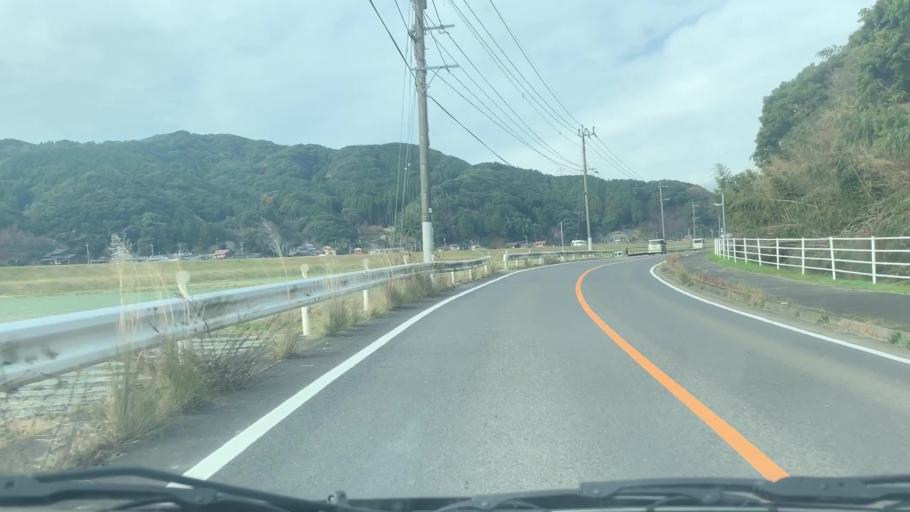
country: JP
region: Saga Prefecture
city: Karatsu
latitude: 33.3801
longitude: 129.9933
